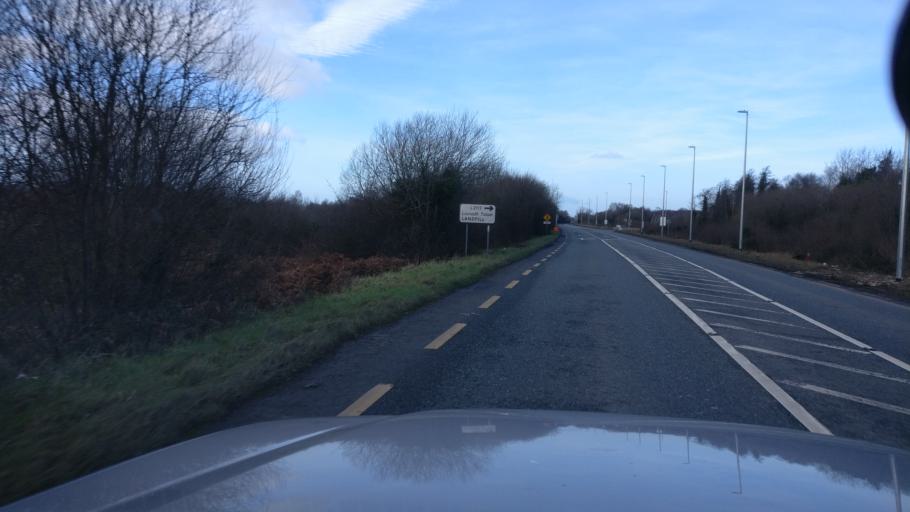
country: IE
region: Leinster
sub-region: Laois
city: Portlaoise
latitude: 53.0655
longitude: -7.3262
